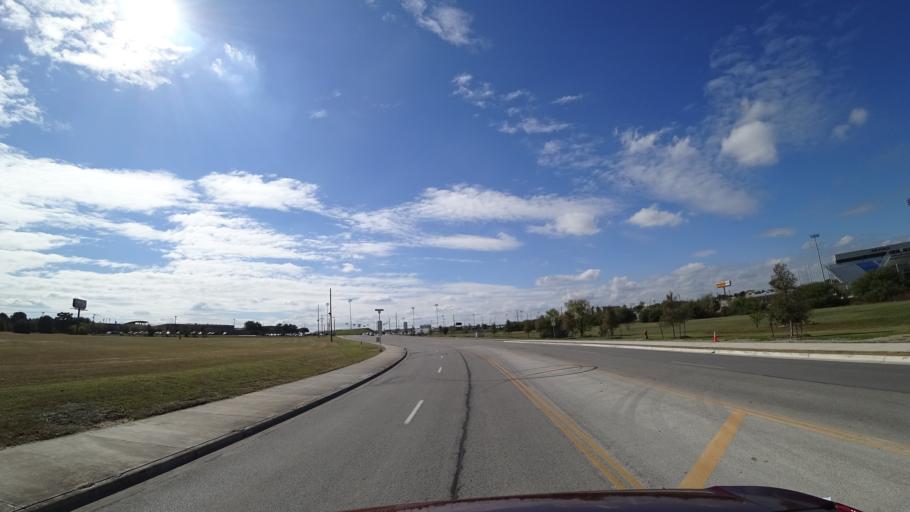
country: US
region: Texas
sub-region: Travis County
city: Pflugerville
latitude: 30.4475
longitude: -97.6323
